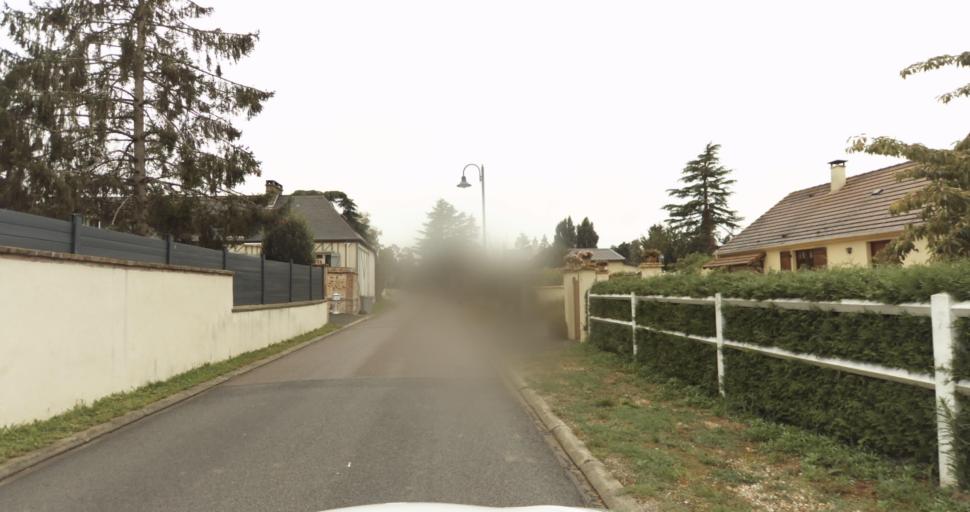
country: FR
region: Haute-Normandie
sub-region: Departement de l'Eure
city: Gravigny
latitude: 49.0829
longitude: 1.2062
